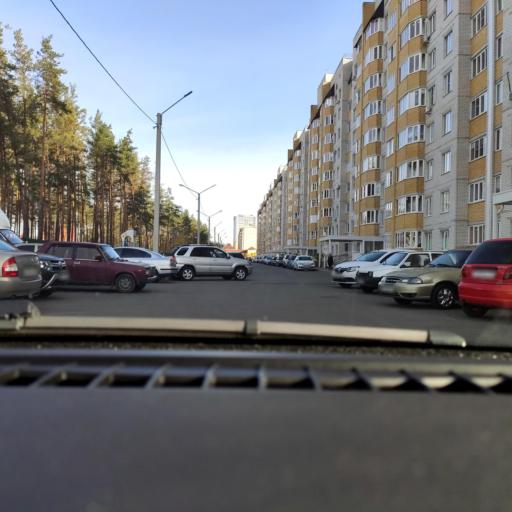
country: RU
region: Voronezj
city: Somovo
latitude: 51.7374
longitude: 39.3171
